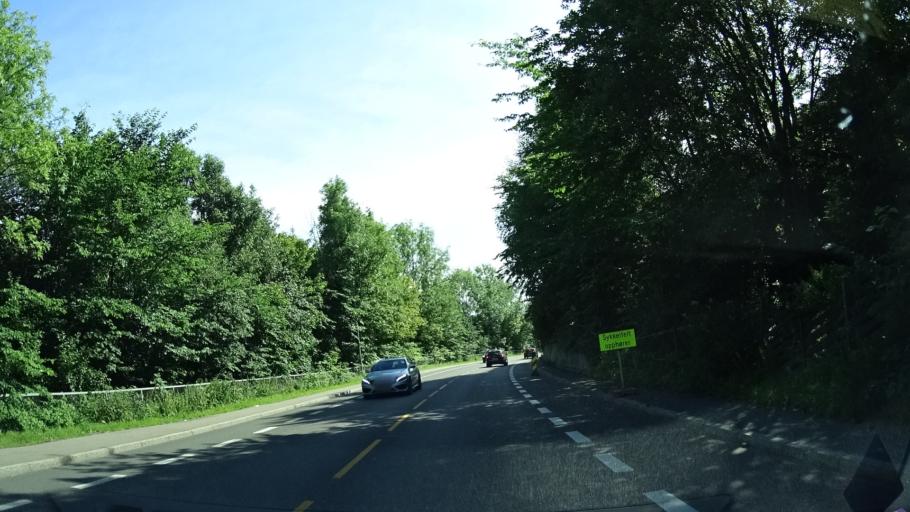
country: NO
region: Oslo
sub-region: Oslo
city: Oslo
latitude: 59.9570
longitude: 10.7637
